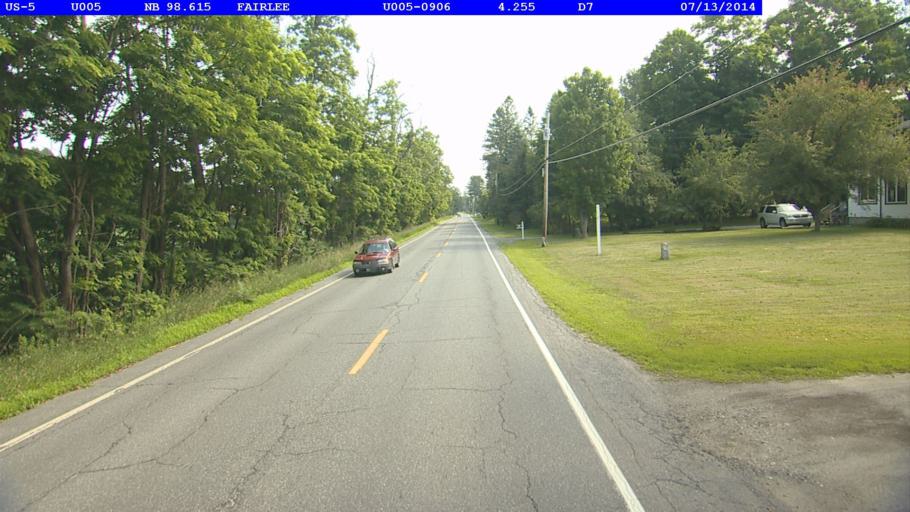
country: US
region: New Hampshire
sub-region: Grafton County
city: Orford
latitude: 43.9194
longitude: -72.1272
